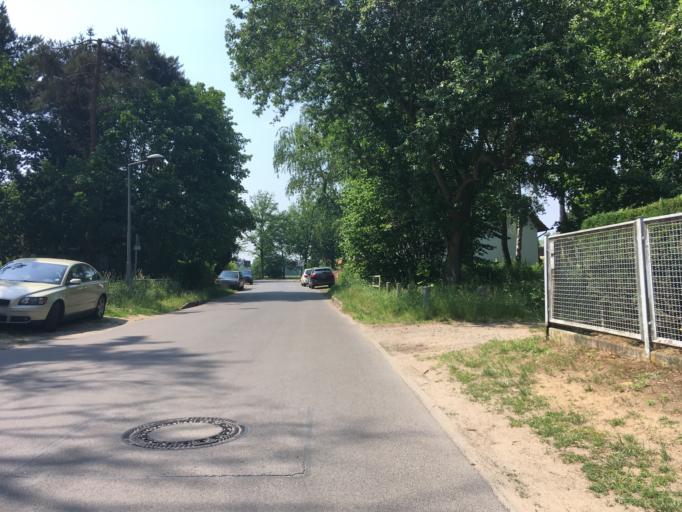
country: DE
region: Berlin
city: Heiligensee
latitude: 52.6145
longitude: 13.2250
